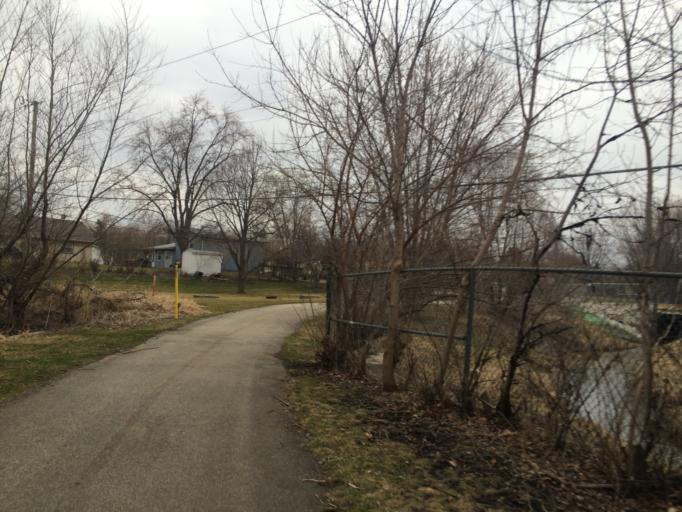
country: US
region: Illinois
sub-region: DuPage County
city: Hanover Park
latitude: 42.0105
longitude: -88.1327
